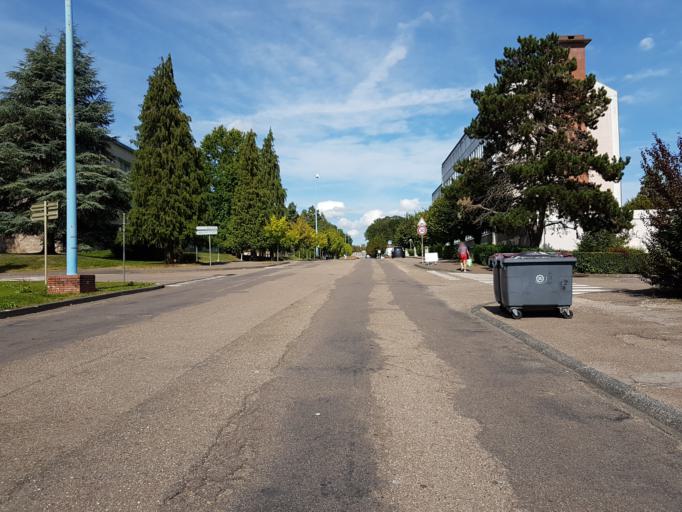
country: FR
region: Franche-Comte
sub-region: Departement de la Haute-Saone
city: Luxeuil-les-Bains
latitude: 47.8174
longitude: 6.3629
